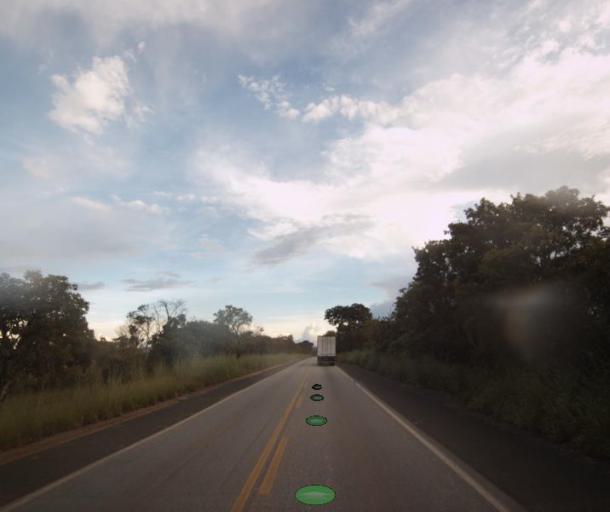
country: BR
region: Goias
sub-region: Uruacu
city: Uruacu
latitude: -14.0523
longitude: -49.0899
